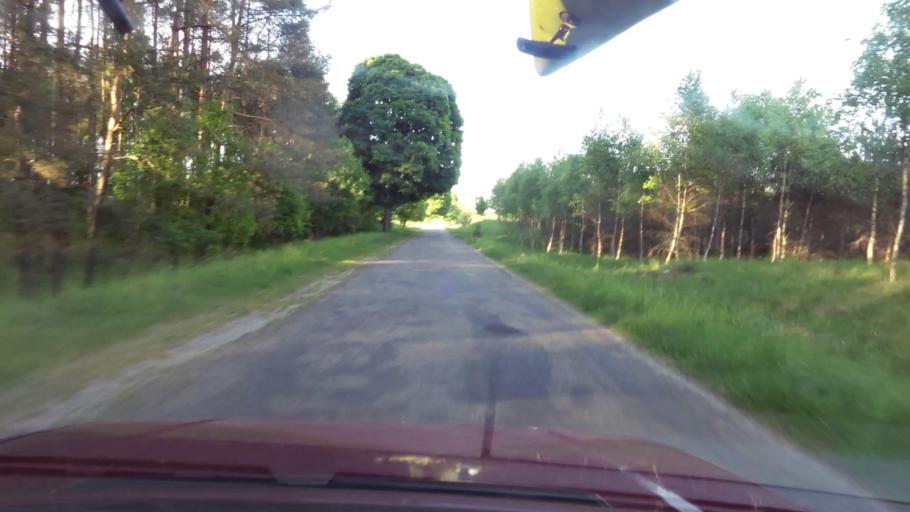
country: PL
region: West Pomeranian Voivodeship
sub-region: Powiat szczecinecki
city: Bialy Bor
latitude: 53.9426
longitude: 16.7651
